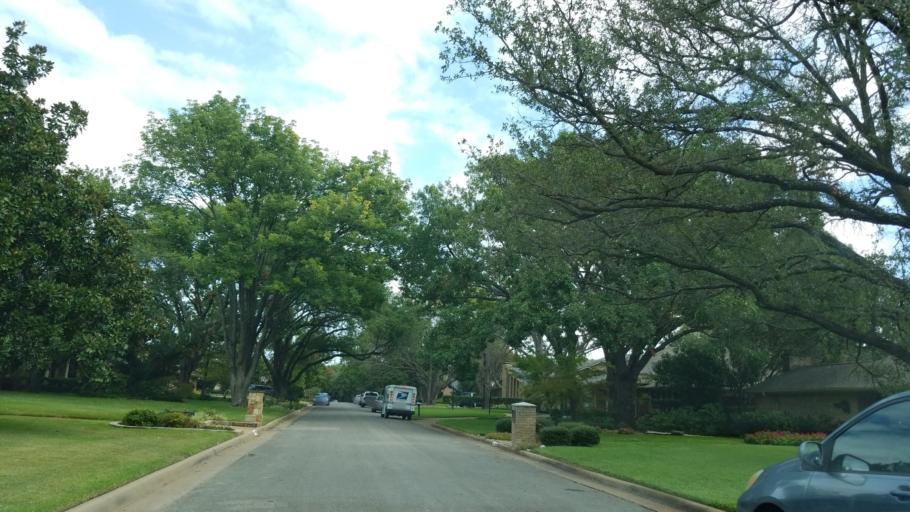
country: US
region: Texas
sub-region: Dallas County
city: Addison
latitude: 32.9466
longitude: -96.7826
